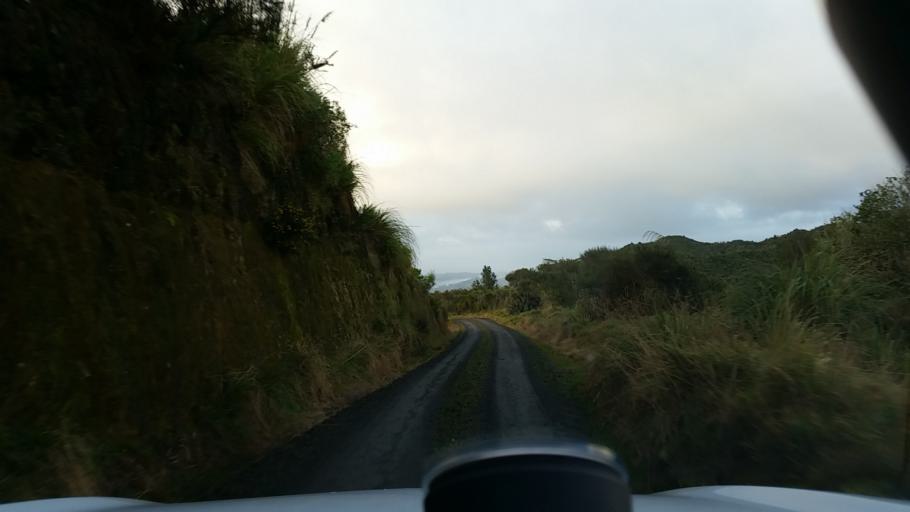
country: NZ
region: Taranaki
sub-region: South Taranaki District
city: Eltham
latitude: -39.4430
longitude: 174.4512
